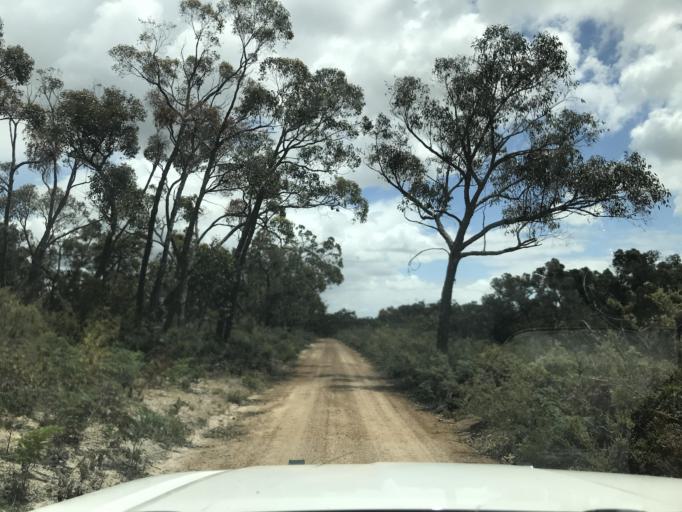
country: AU
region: South Australia
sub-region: Wattle Range
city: Penola
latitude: -37.0892
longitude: 141.3374
